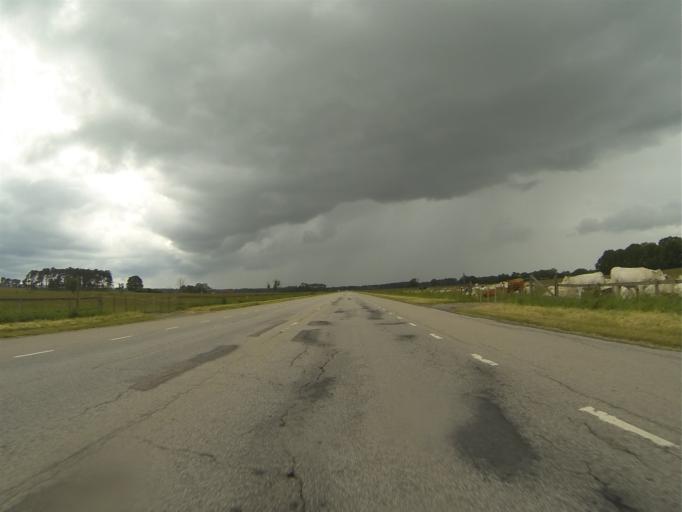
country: SE
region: Skane
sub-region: Hoors Kommun
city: Loberod
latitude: 55.7272
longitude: 13.4376
